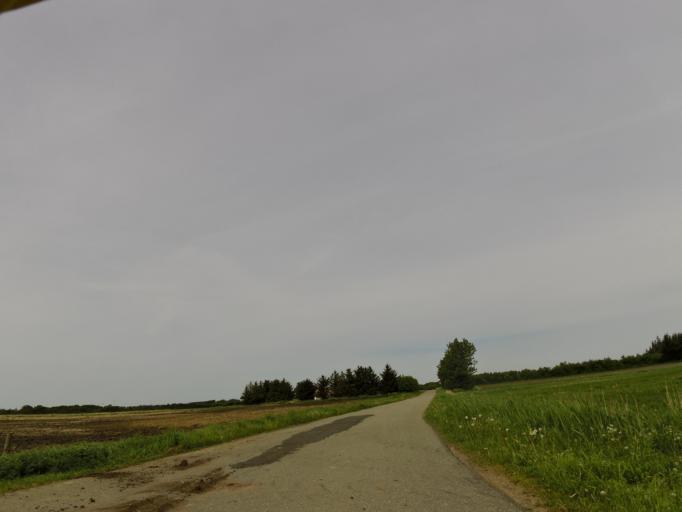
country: DK
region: Central Jutland
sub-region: Holstebro Kommune
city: Vinderup
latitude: 56.5506
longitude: 8.8872
